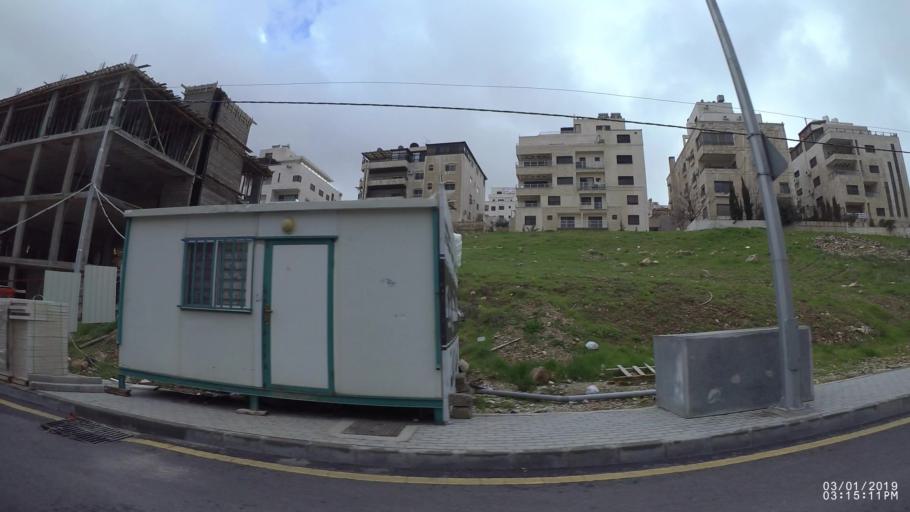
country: JO
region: Amman
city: Amman
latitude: 31.9525
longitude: 35.8911
